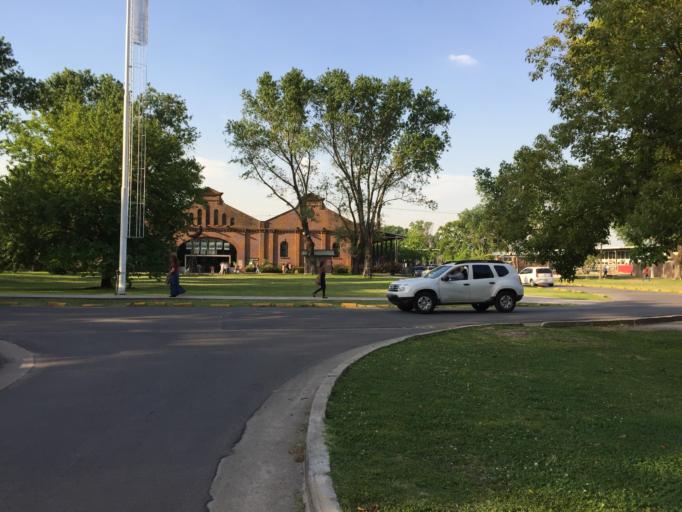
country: AR
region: Buenos Aires
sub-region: Partido de Lomas de Zamora
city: Lomas de Zamora
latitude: -34.7343
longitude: -58.3937
